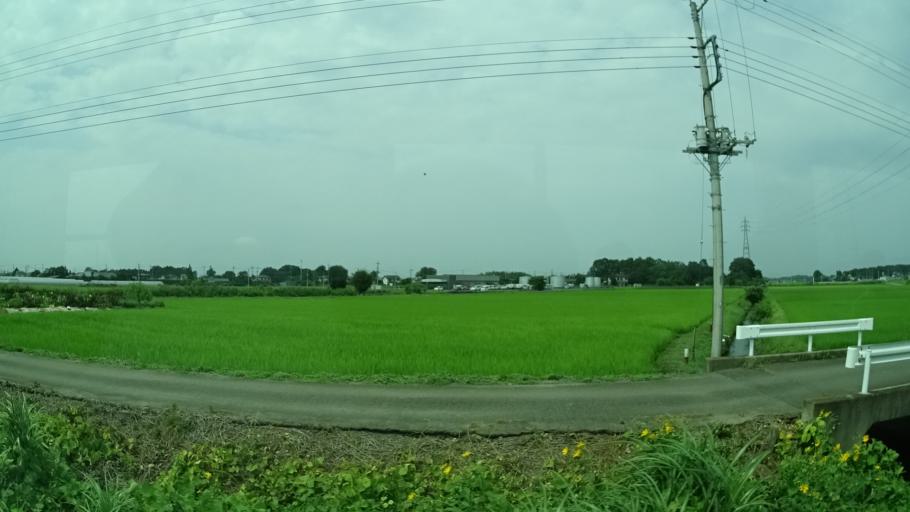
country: JP
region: Tochigi
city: Mooka
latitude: 36.4520
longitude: 140.0372
